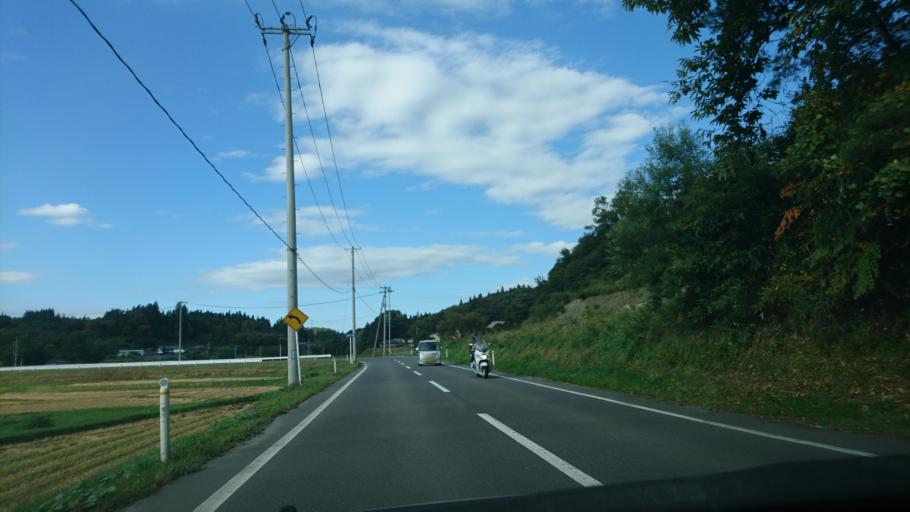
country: JP
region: Iwate
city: Ichinoseki
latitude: 38.8765
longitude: 141.3429
